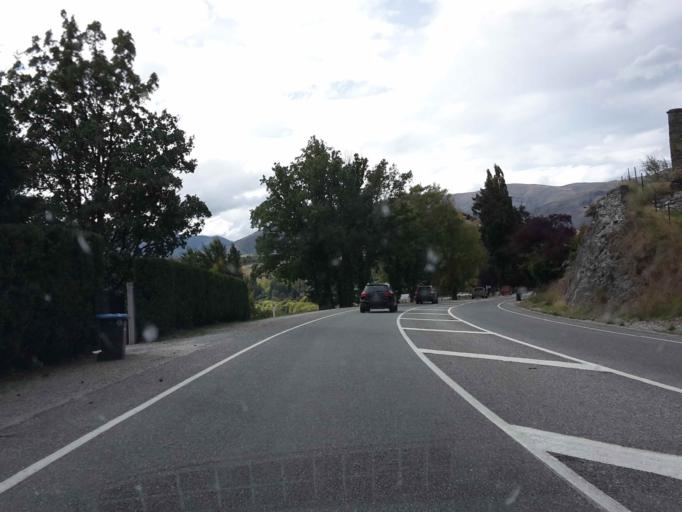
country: NZ
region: Otago
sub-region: Queenstown-Lakes District
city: Arrowtown
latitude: -44.9919
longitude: 168.8074
